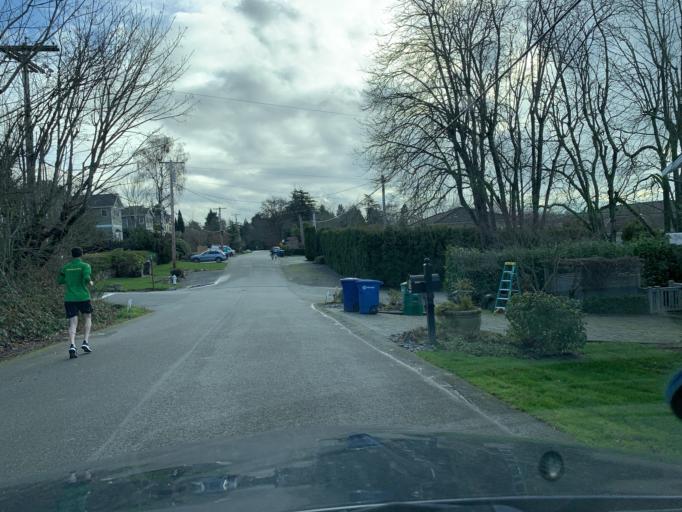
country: US
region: Washington
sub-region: King County
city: Mercer Island
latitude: 47.5856
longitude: -122.2525
